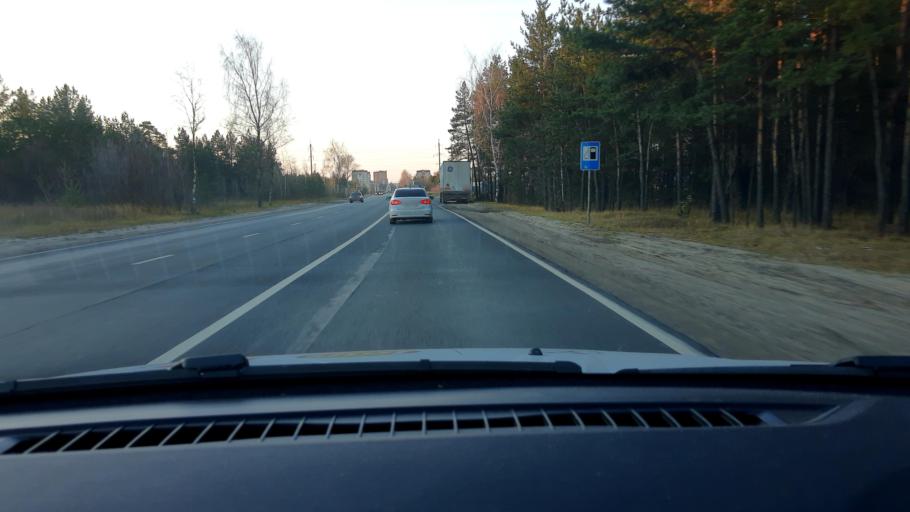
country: RU
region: Nizjnij Novgorod
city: Dzerzhinsk
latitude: 56.2638
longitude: 43.4692
